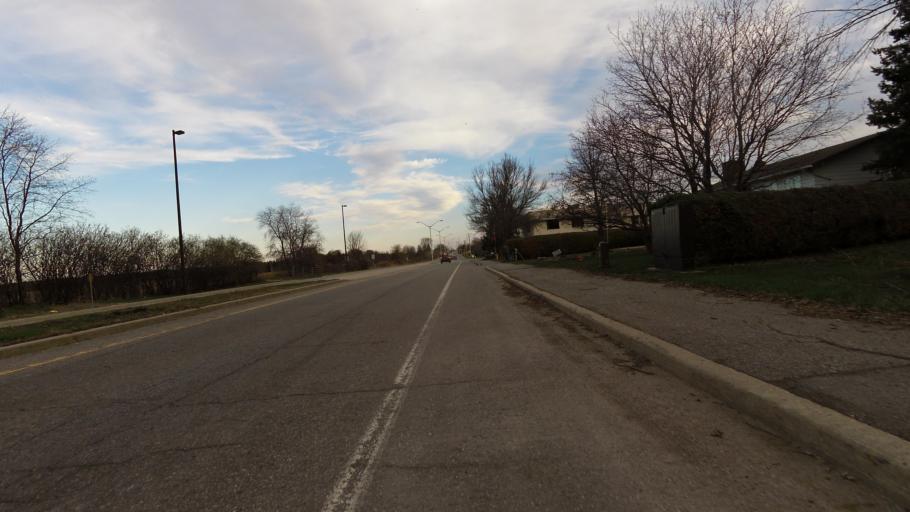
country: CA
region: Ontario
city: Bells Corners
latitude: 45.3437
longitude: -75.9001
